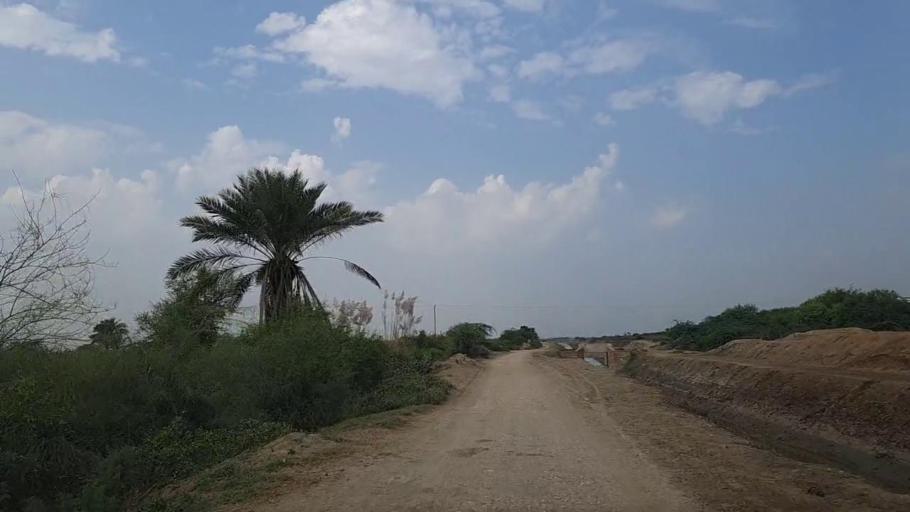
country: PK
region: Sindh
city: Daro Mehar
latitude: 24.7196
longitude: 68.1387
